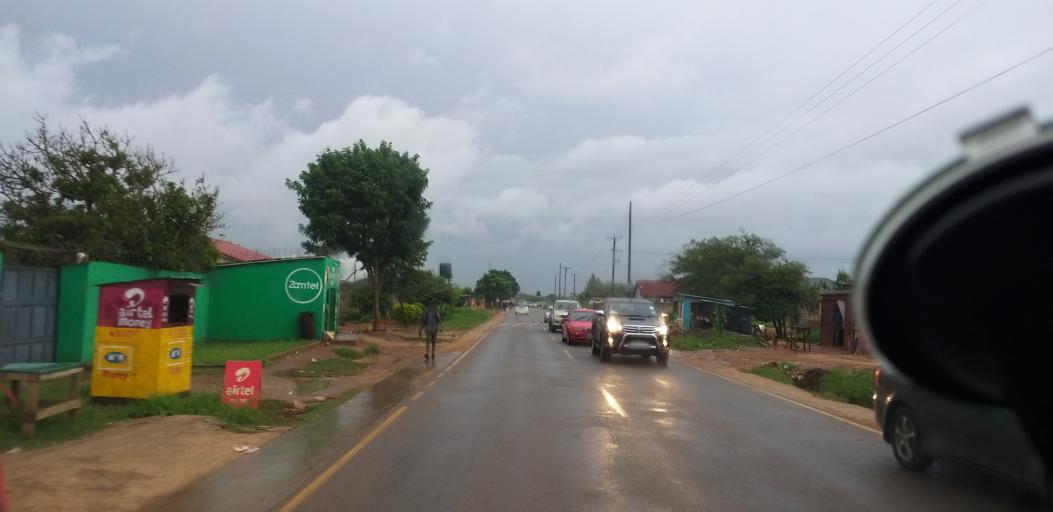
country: ZM
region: Lusaka
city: Lusaka
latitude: -15.4976
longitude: 28.3127
